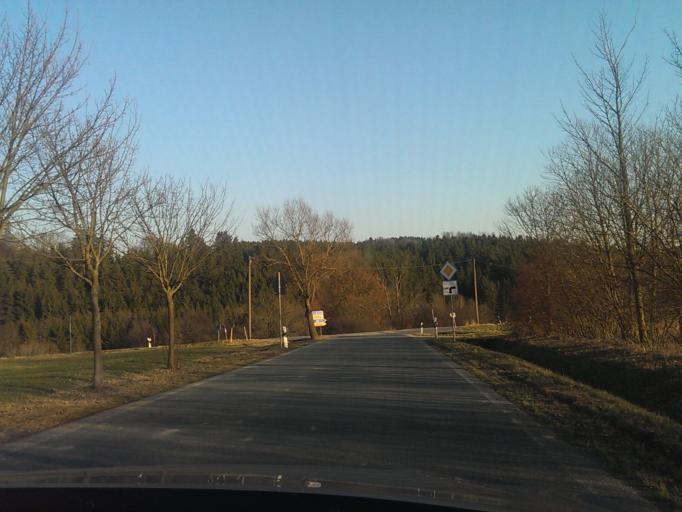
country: DE
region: Bavaria
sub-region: Upper Franconia
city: Gattendorf
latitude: 50.3785
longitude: 12.0152
